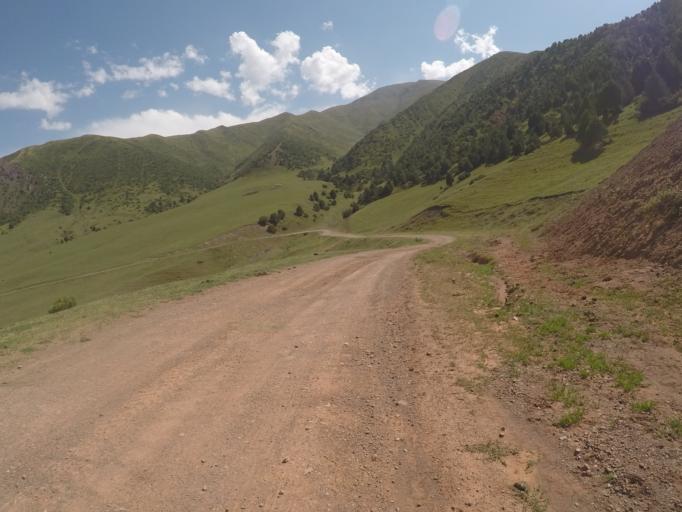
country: KG
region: Chuy
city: Bishkek
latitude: 42.6452
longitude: 74.5700
